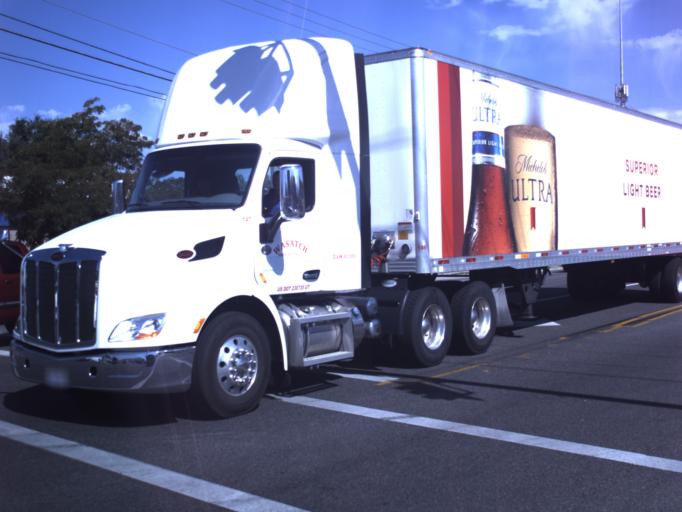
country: US
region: Utah
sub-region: Davis County
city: Clearfield
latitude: 41.1181
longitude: -112.0260
